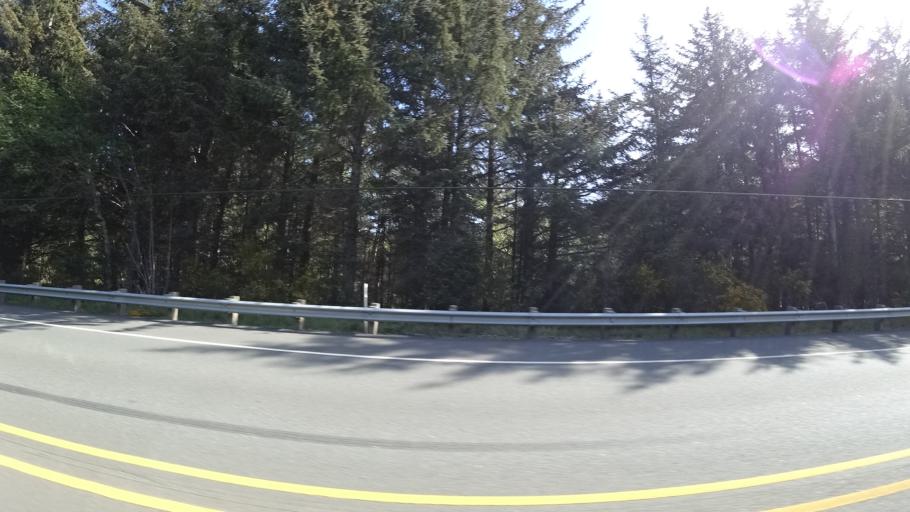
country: US
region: Oregon
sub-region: Curry County
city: Gold Beach
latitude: 42.2344
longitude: -124.3877
